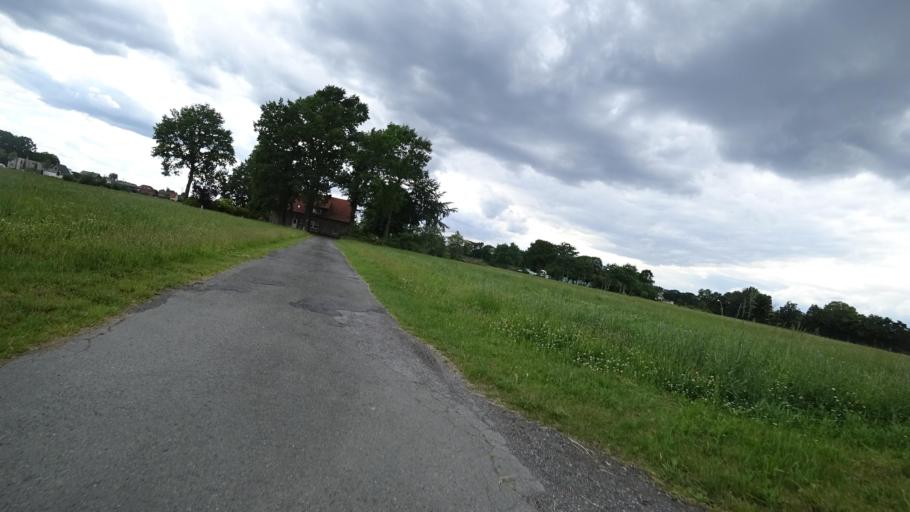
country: DE
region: North Rhine-Westphalia
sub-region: Regierungsbezirk Detmold
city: Guetersloh
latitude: 51.8933
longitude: 8.4411
